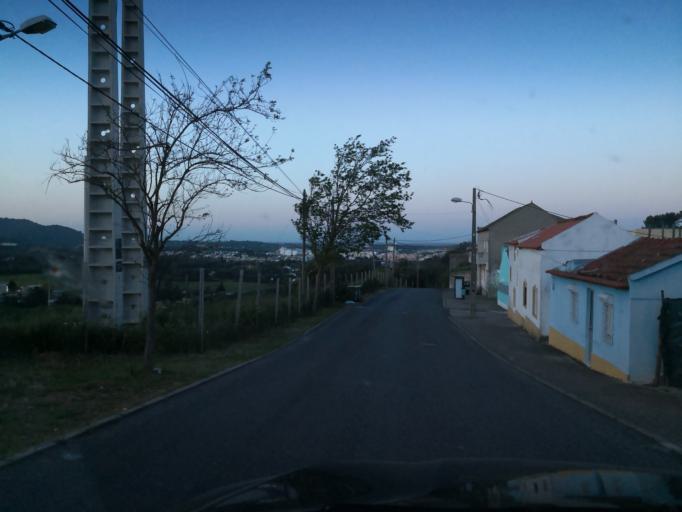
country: PT
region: Setubal
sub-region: Setubal
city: Setubal
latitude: 38.5280
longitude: -8.9111
